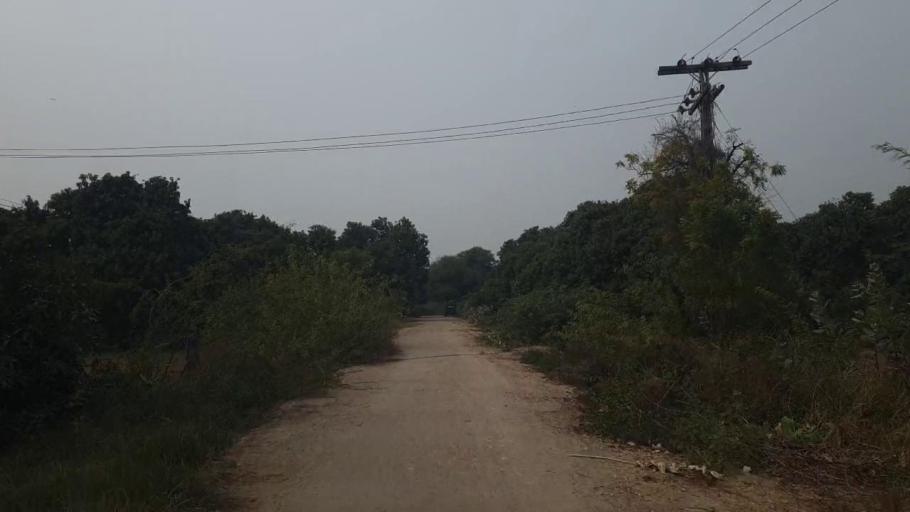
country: PK
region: Sindh
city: Tando Adam
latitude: 25.7868
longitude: 68.6644
